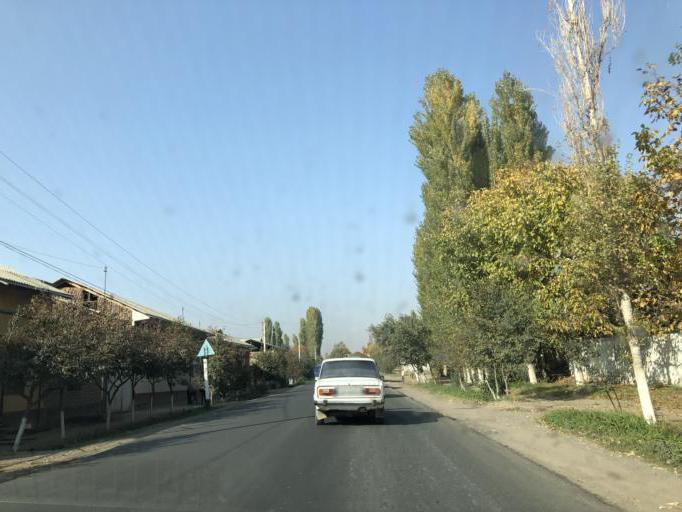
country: UZ
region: Namangan
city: Chust Shahri
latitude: 41.0691
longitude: 71.2046
